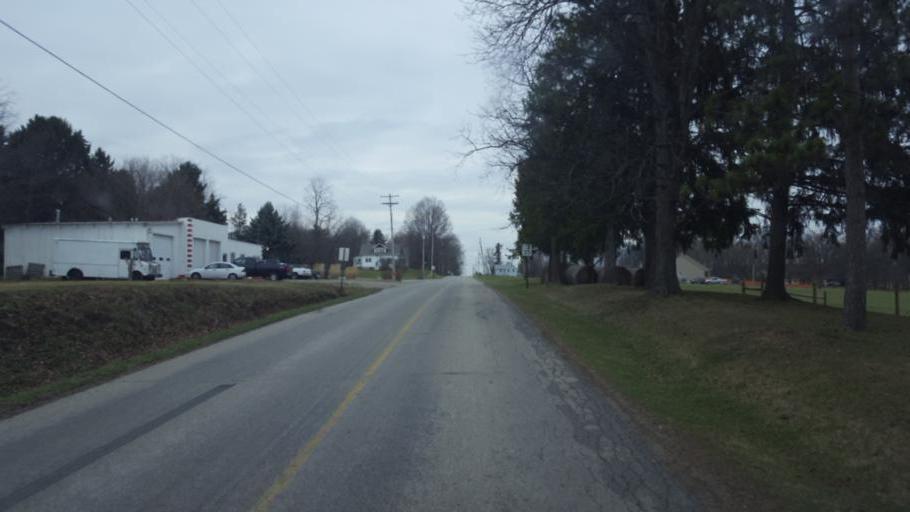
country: US
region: Ohio
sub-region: Richland County
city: Lincoln Heights
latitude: 40.7031
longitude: -82.4731
